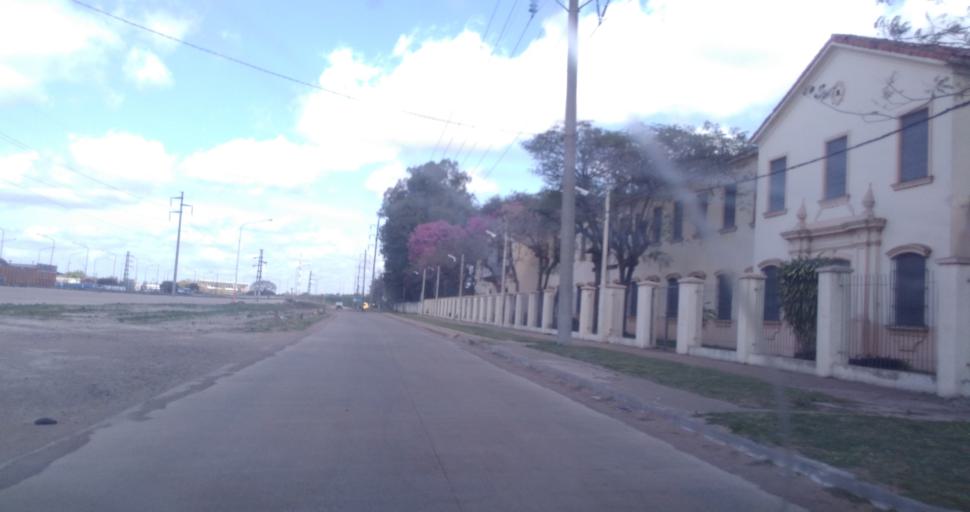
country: AR
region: Chaco
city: Fontana
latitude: -27.4310
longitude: -59.0110
